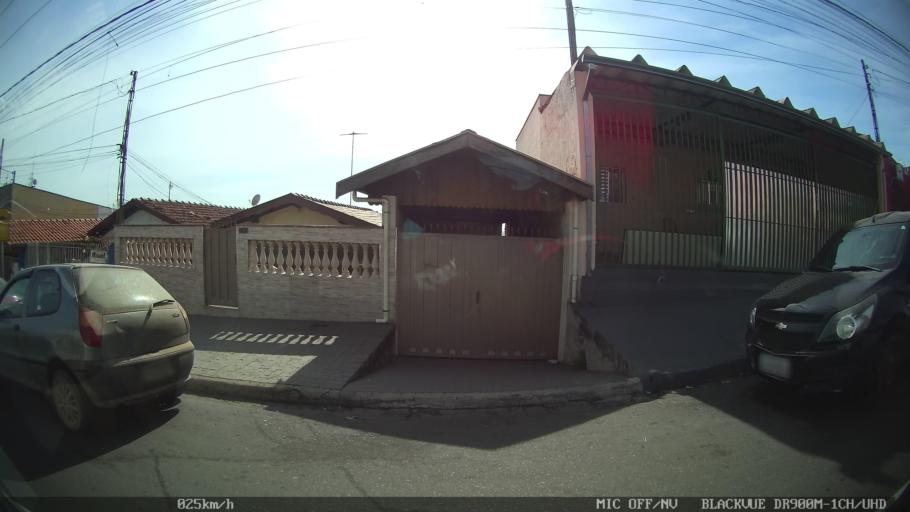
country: BR
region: Sao Paulo
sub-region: Piracicaba
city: Piracicaba
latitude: -22.7469
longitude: -47.6595
